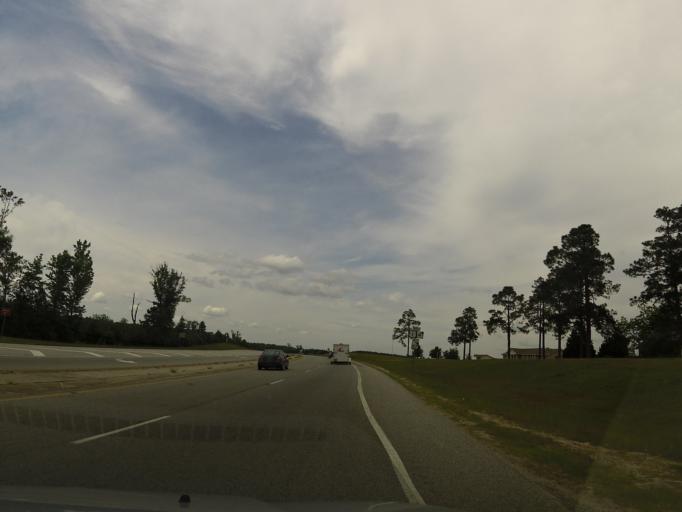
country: US
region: Georgia
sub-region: Emanuel County
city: Swainsboro
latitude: 32.5250
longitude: -82.3007
